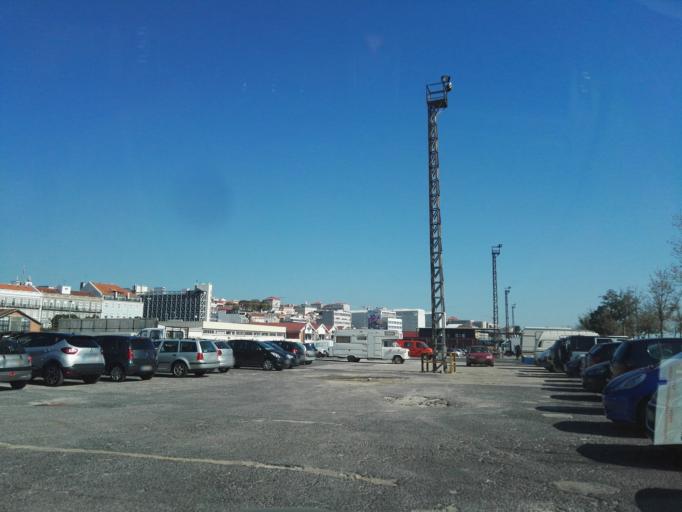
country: PT
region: Setubal
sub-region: Almada
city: Cacilhas
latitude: 38.7049
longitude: -9.1548
